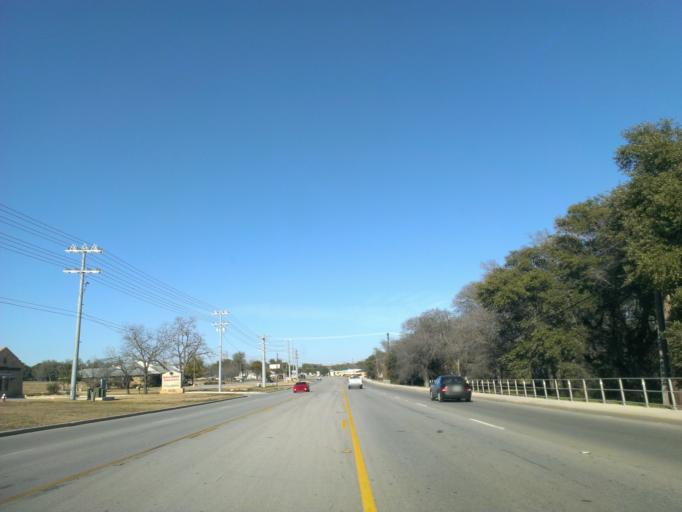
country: US
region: Texas
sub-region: Burnet County
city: Burnet
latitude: 30.7456
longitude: -98.2313
